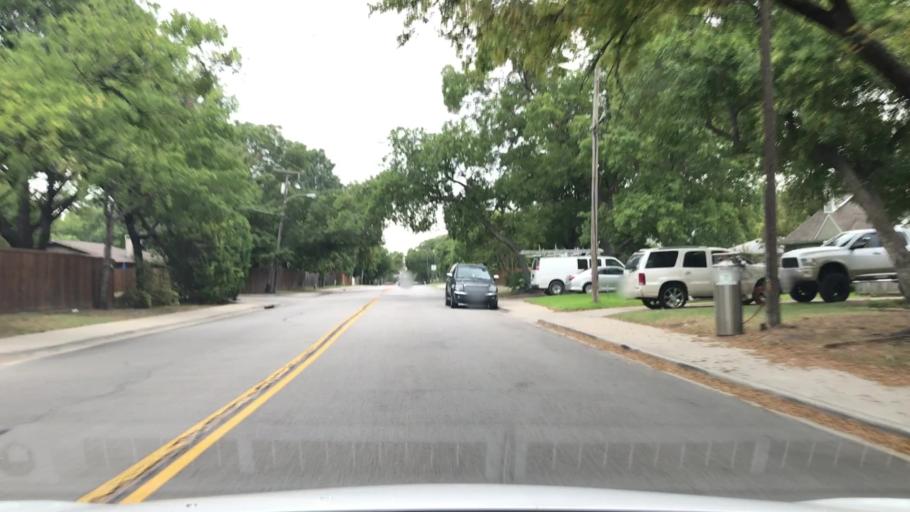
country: US
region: Texas
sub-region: Dallas County
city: Carrollton
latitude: 32.9645
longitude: -96.9074
